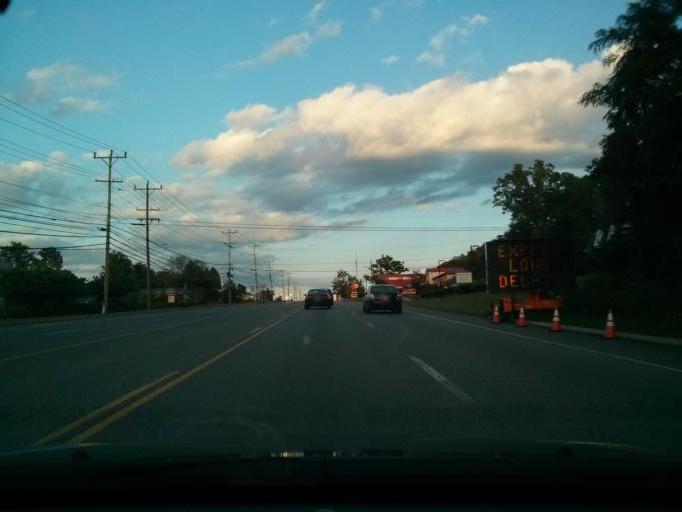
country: US
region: Pennsylvania
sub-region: Centre County
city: Park Forest Village
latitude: 40.8100
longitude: -77.9128
